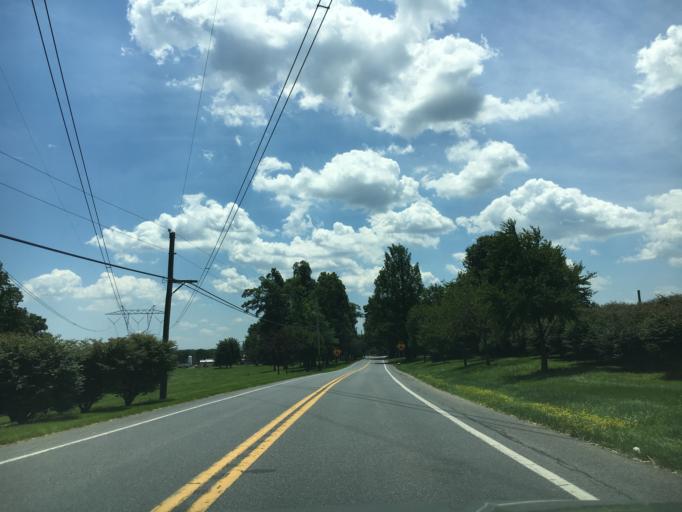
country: US
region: Pennsylvania
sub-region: Lehigh County
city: Schnecksville
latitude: 40.6474
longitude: -75.5780
